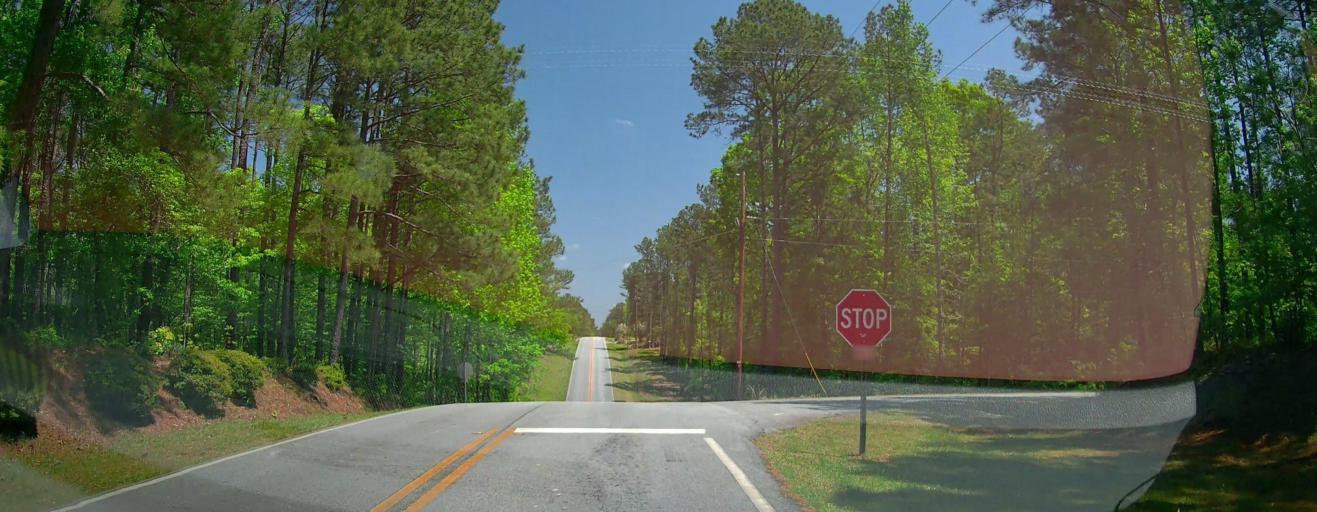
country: US
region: Georgia
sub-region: Jones County
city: Gray
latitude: 32.9461
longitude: -83.5752
